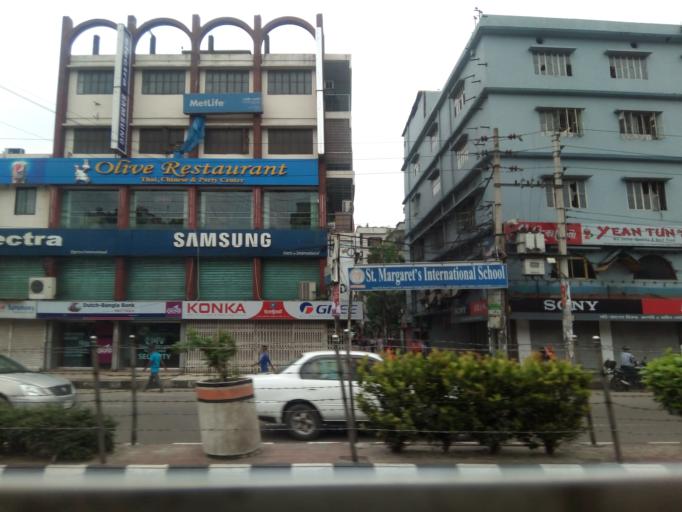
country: BD
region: Dhaka
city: Azimpur
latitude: 23.7619
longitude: 90.3892
